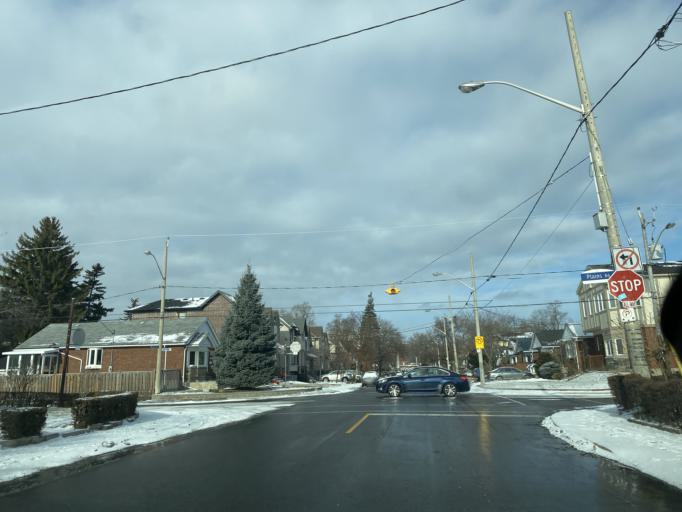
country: CA
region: Ontario
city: Toronto
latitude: 43.6936
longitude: -79.3384
